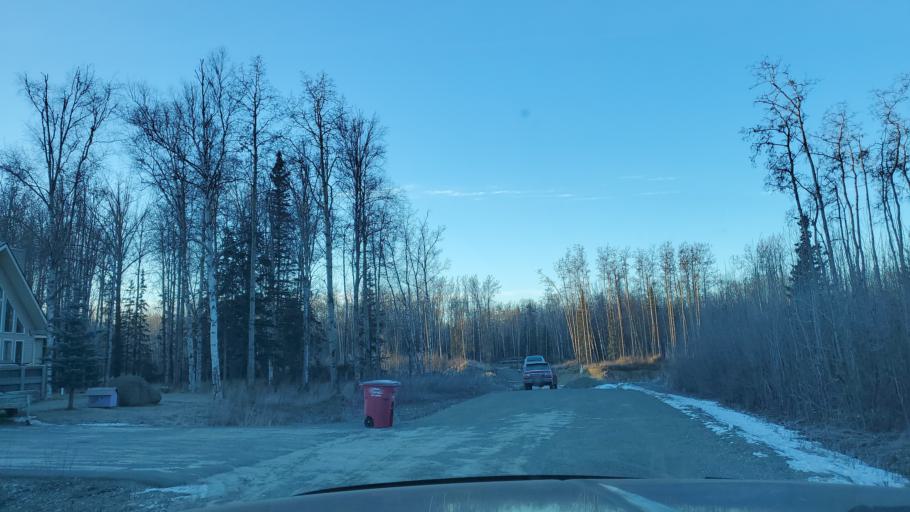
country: US
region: Alaska
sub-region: Matanuska-Susitna Borough
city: Lakes
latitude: 61.6558
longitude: -149.3404
